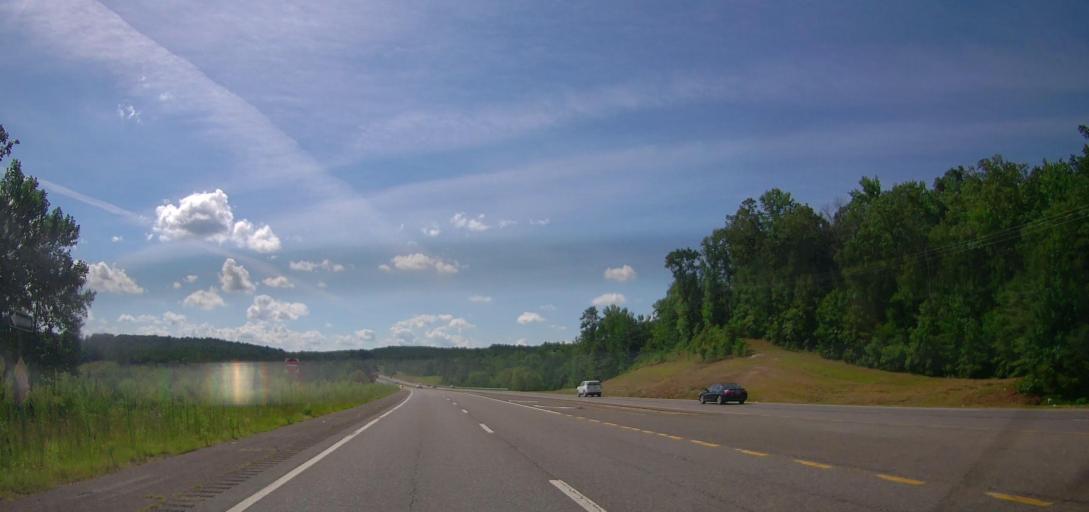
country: US
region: Alabama
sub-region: Tuscaloosa County
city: Northport
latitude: 33.2640
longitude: -87.7102
